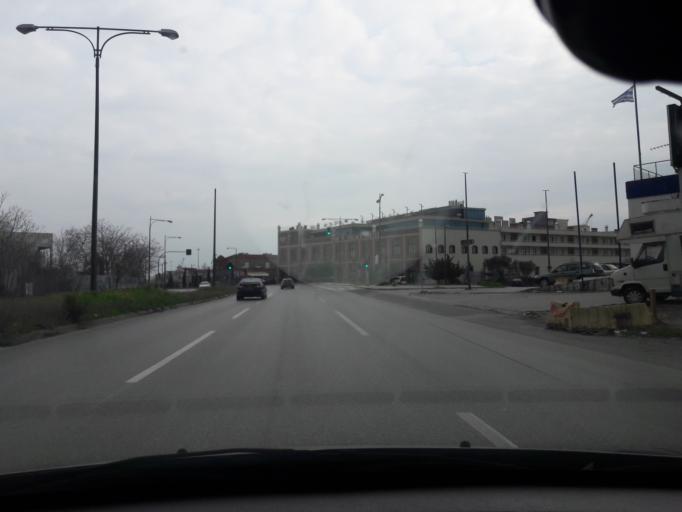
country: GR
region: Central Macedonia
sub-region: Nomos Thessalonikis
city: Menemeni
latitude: 40.6444
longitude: 22.9096
